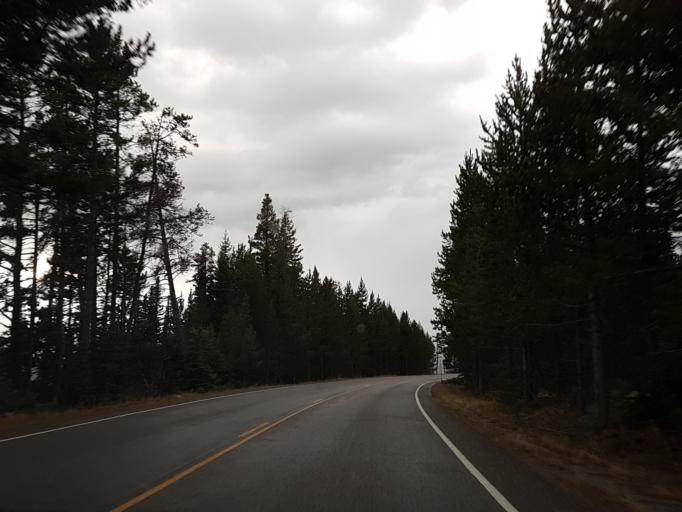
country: US
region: Montana
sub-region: Gallatin County
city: West Yellowstone
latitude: 44.4531
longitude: -110.5000
